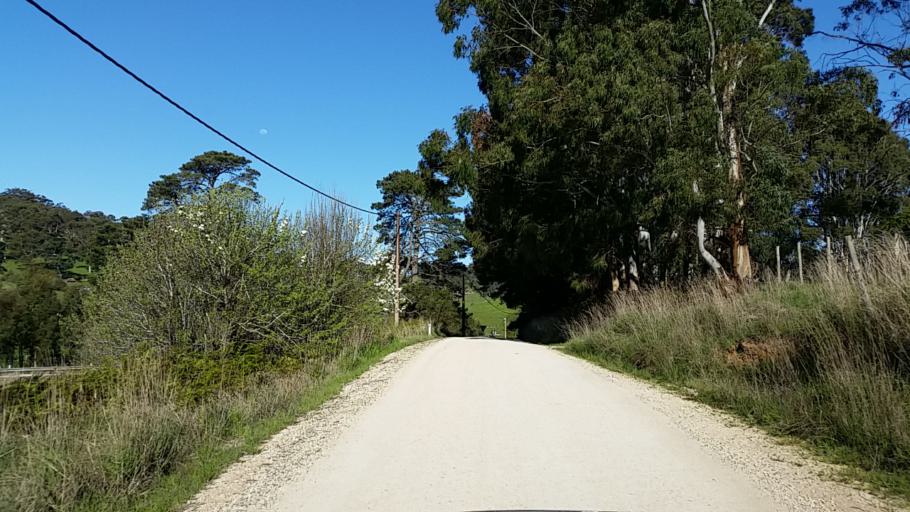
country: AU
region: South Australia
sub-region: Adelaide Hills
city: Lobethal
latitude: -34.8916
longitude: 138.8554
